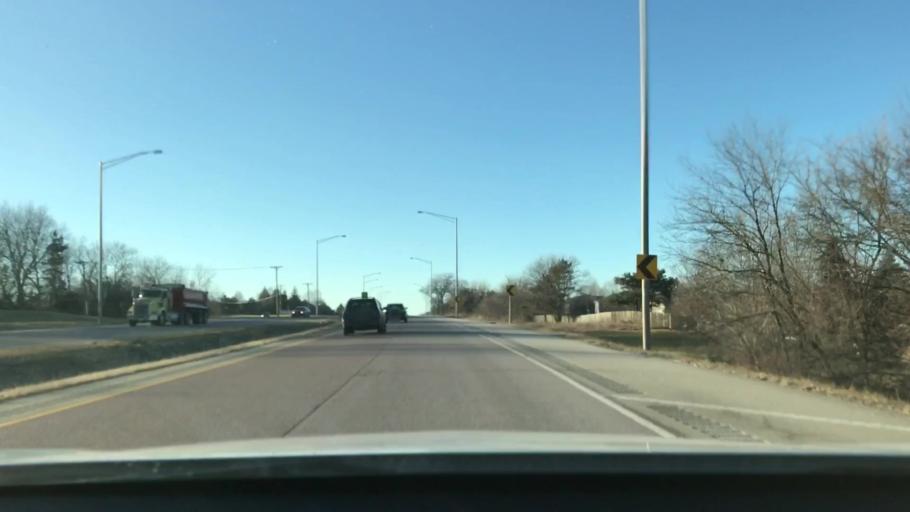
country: US
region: Illinois
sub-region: Kane County
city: Elgin
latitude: 42.0355
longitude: -88.3482
